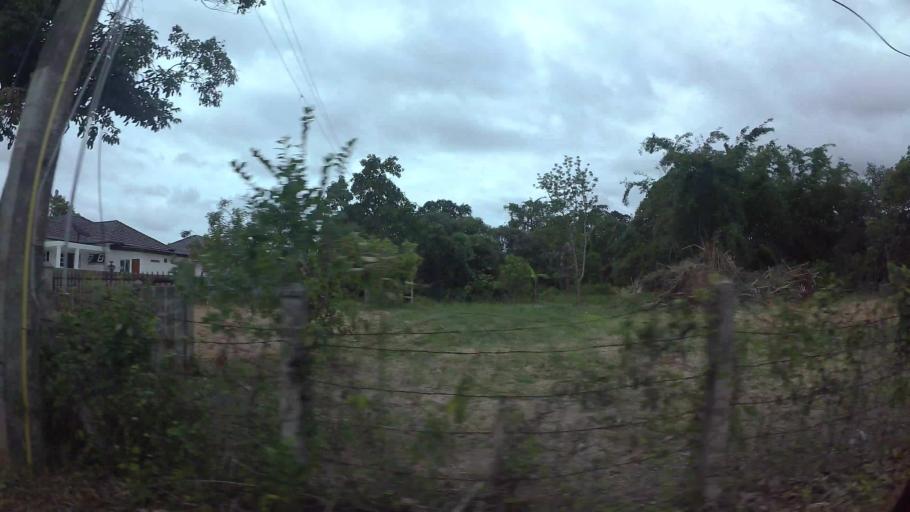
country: TH
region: Chon Buri
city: Sattahip
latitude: 12.7247
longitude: 100.9008
